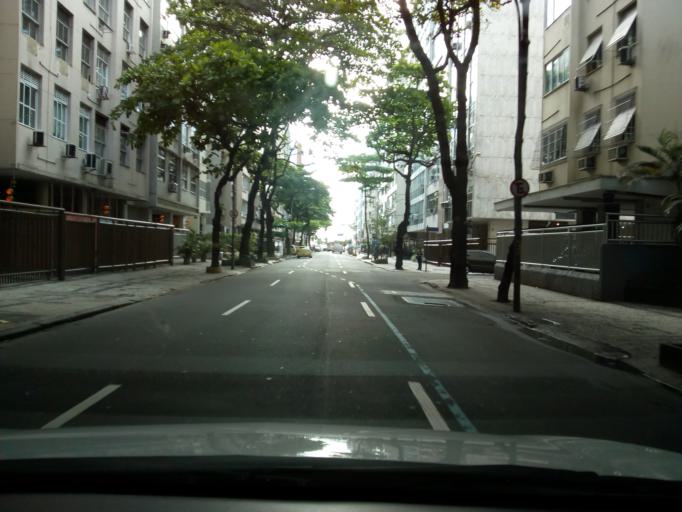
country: BR
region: Rio de Janeiro
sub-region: Rio De Janeiro
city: Rio de Janeiro
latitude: -22.9860
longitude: -43.1945
